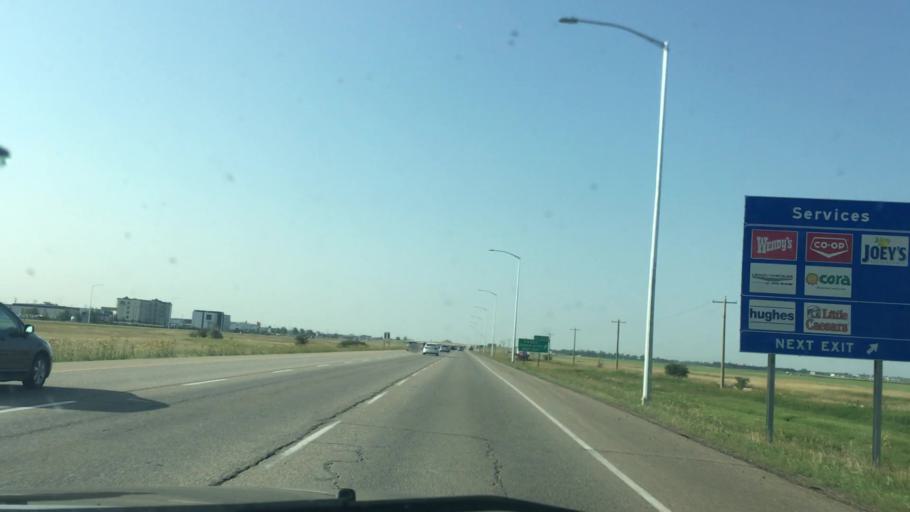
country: CA
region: Alberta
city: Leduc
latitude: 53.2988
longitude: -113.5499
